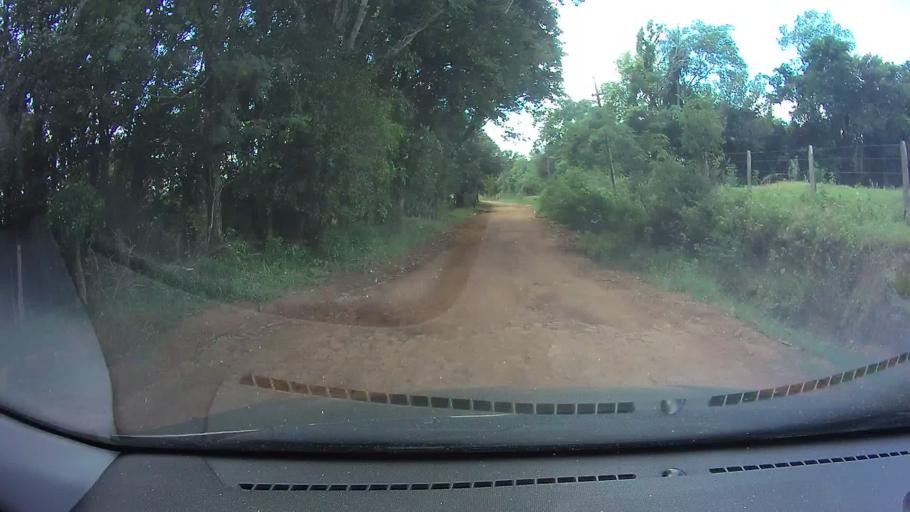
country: PY
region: Paraguari
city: La Colmena
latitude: -25.9348
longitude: -56.7839
